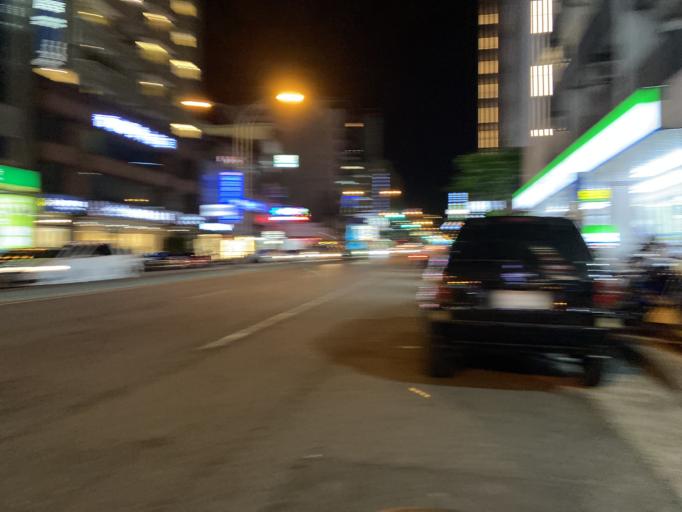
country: TW
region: Taiwan
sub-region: Taichung City
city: Taichung
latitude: 24.1526
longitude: 120.6805
